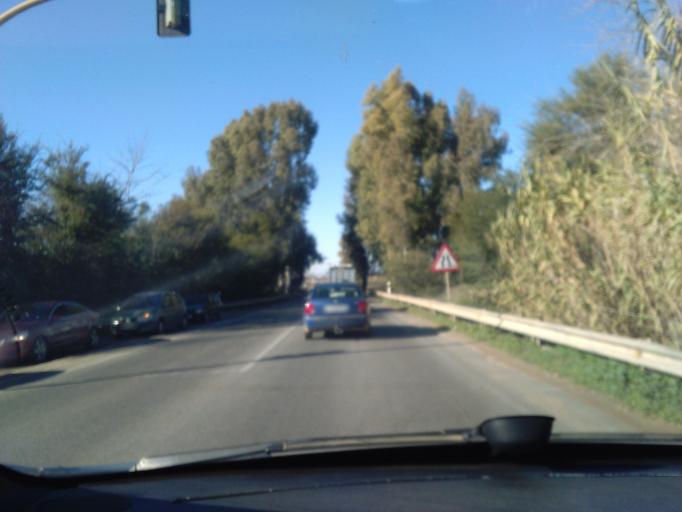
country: ES
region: Andalusia
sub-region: Provincia de Sevilla
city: Sevilla
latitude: 37.4292
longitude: -5.9314
